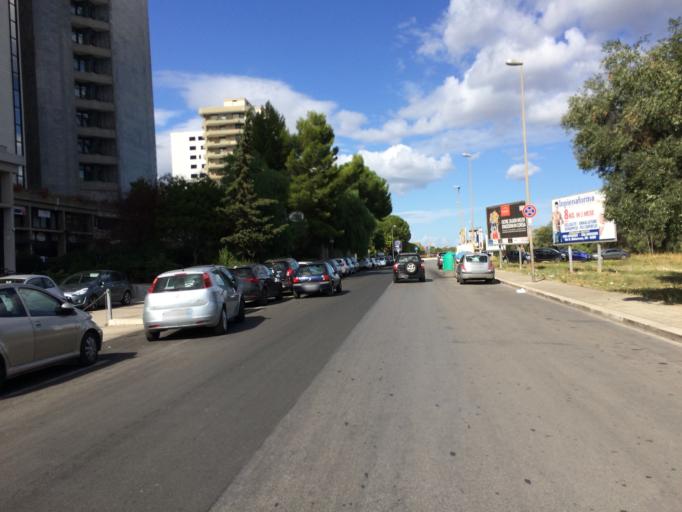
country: IT
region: Apulia
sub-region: Provincia di Bari
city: Bari
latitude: 41.0993
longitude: 16.8559
